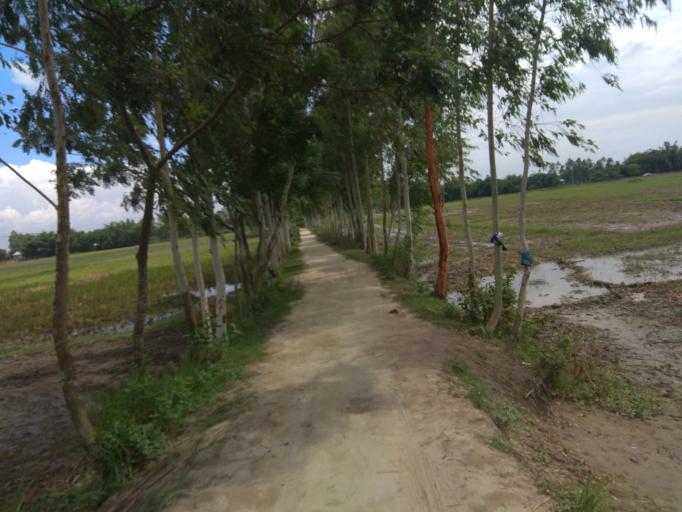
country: IN
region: West Bengal
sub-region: Koch Bihar
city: Haldibari
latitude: 26.1179
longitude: 88.9259
